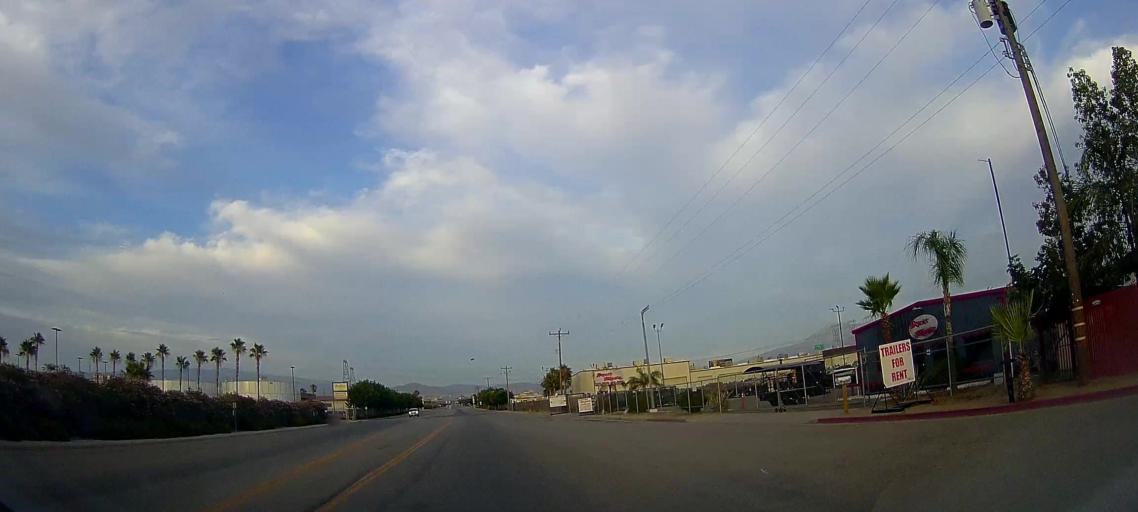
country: US
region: California
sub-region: Kern County
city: Bakersfield
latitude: 35.3543
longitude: -118.9273
